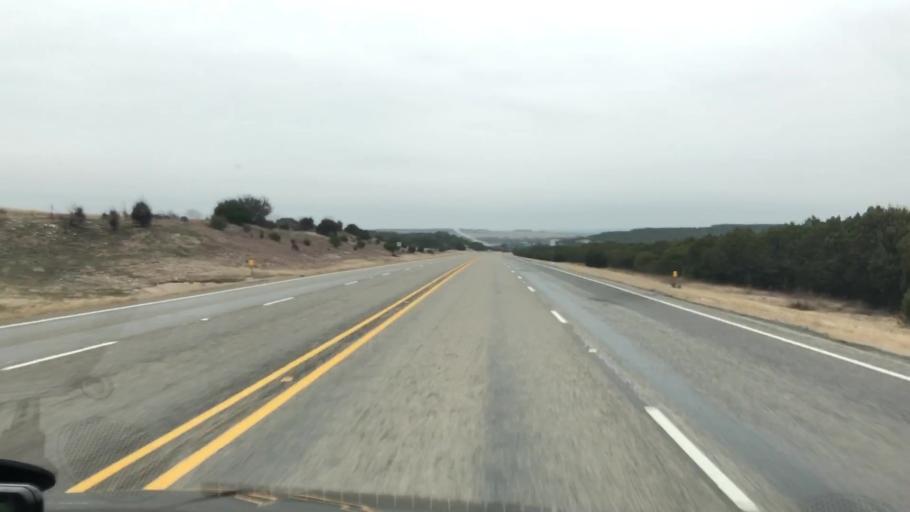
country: US
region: Texas
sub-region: Lampasas County
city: Lampasas
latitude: 31.1959
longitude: -98.1720
